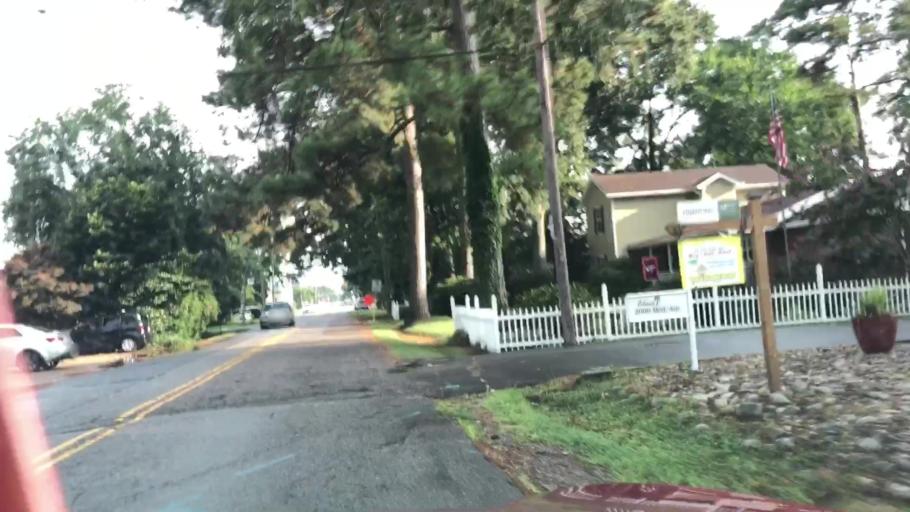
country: US
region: Virginia
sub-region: City of Virginia Beach
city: Virginia Beach
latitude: 36.8477
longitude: -75.9821
